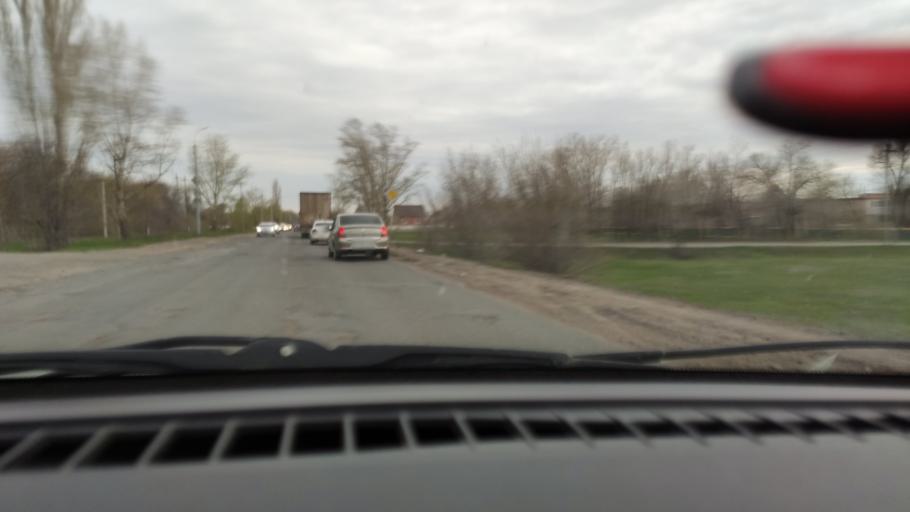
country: RU
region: Orenburg
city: Tatarskaya Kargala
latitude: 51.8656
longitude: 55.1397
